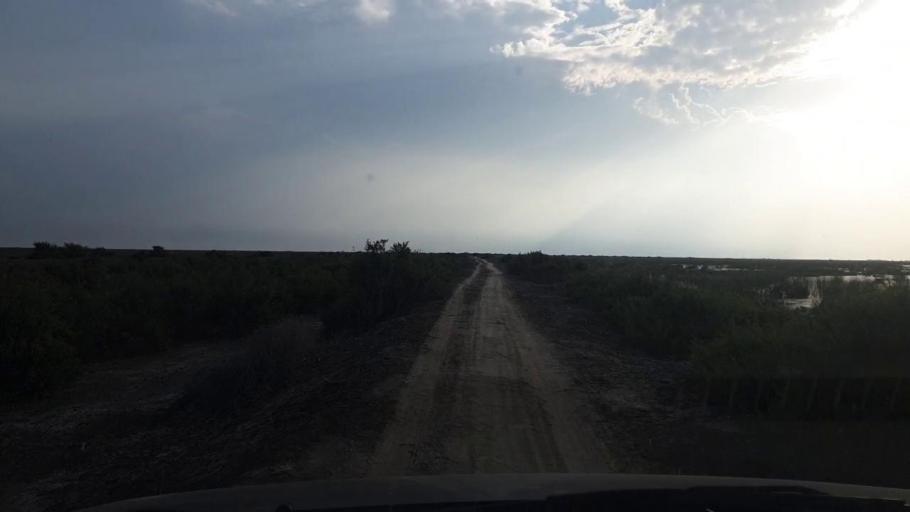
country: PK
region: Sindh
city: Badin
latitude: 24.4351
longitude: 68.6719
